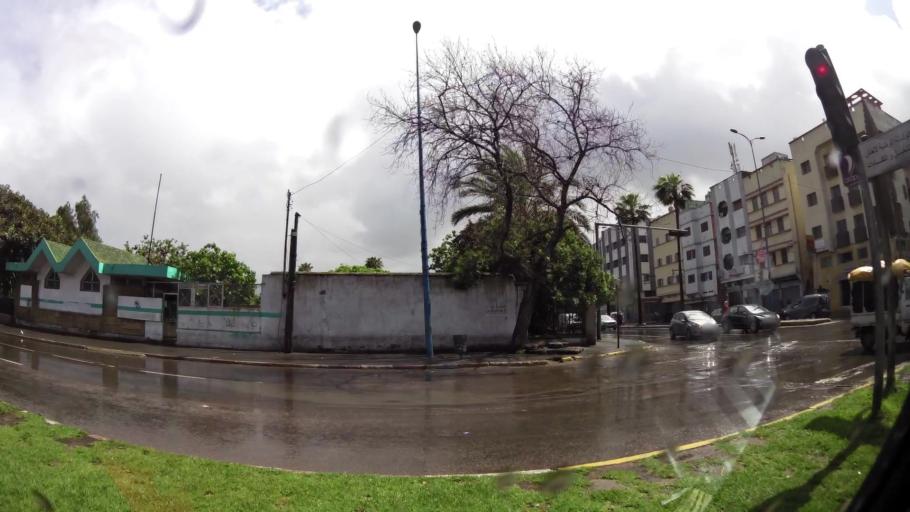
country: MA
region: Grand Casablanca
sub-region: Casablanca
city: Casablanca
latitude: 33.5511
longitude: -7.5682
